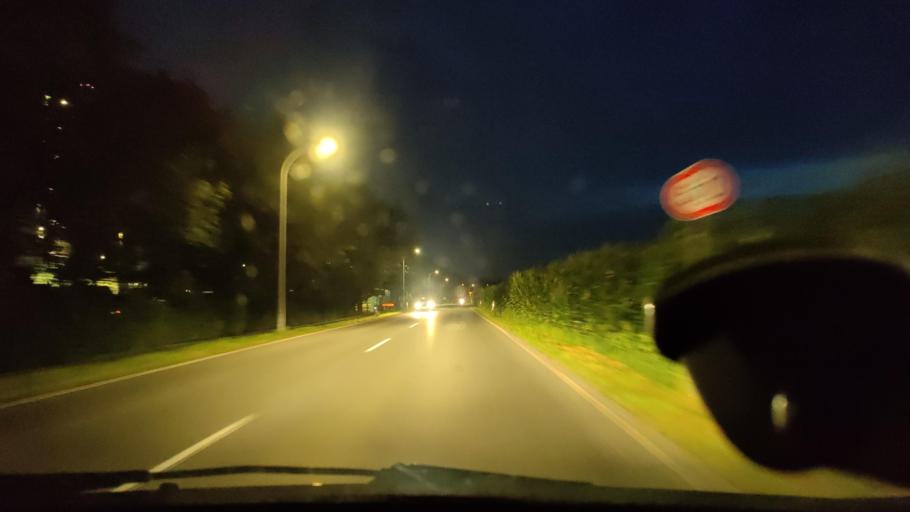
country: DE
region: North Rhine-Westphalia
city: Rheinberg
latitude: 51.5682
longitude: 6.5789
